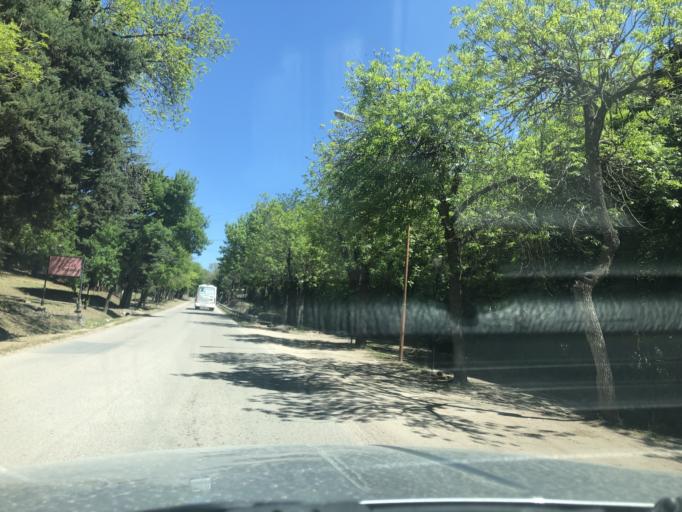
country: AR
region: Cordoba
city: La Granja
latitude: -31.0088
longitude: -64.2687
